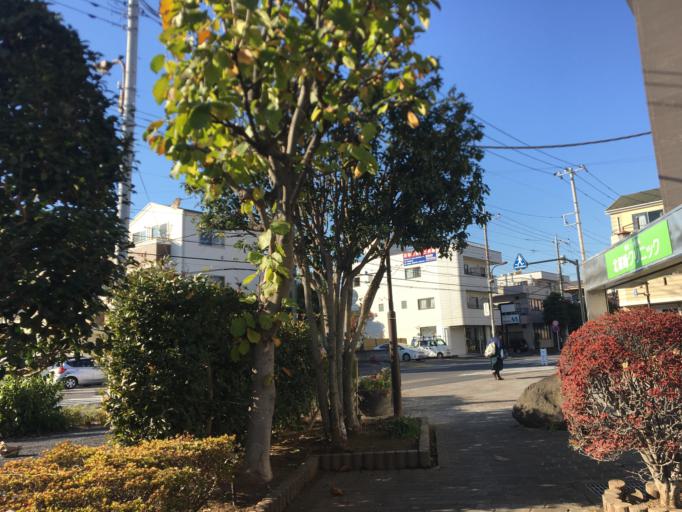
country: JP
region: Tokyo
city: Urayasu
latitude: 35.7175
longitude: 139.8920
